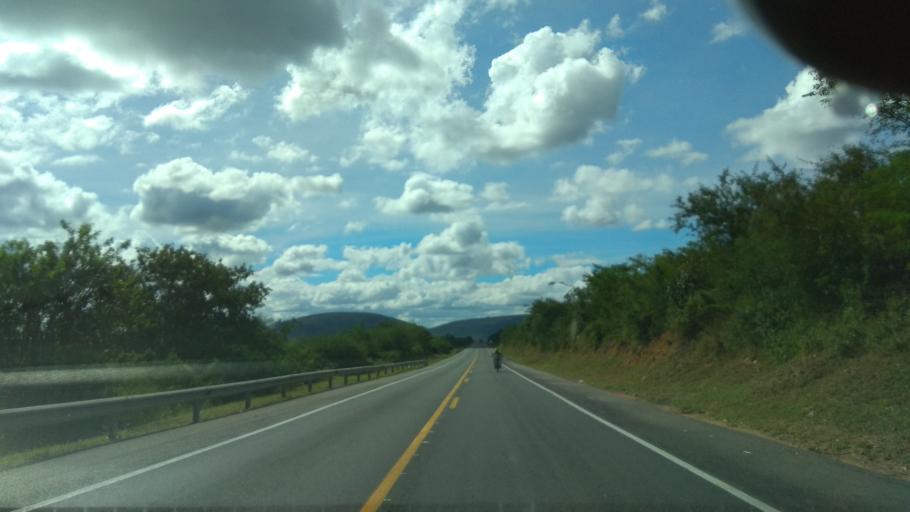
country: BR
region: Bahia
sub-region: Santa Ines
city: Santa Ines
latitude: -13.3042
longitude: -40.0262
